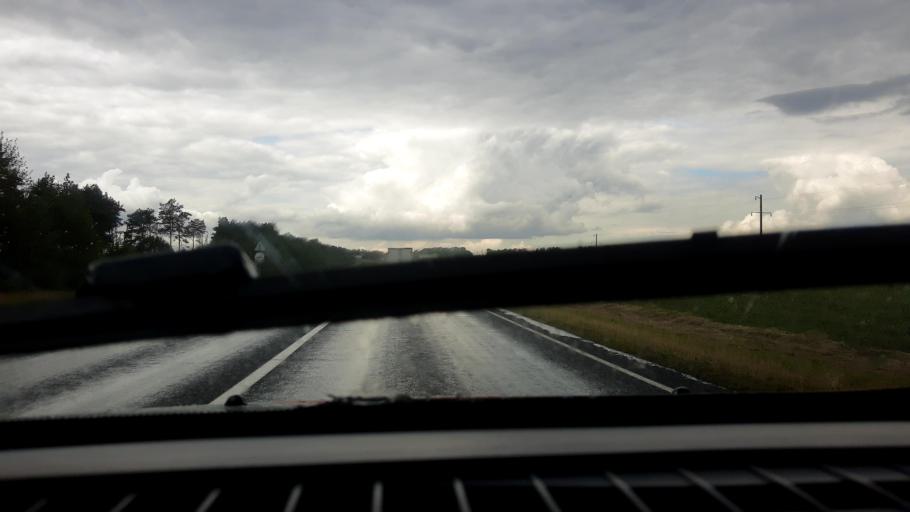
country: RU
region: Nizjnij Novgorod
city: Bol'shoye Murashkino
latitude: 55.8961
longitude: 44.7304
